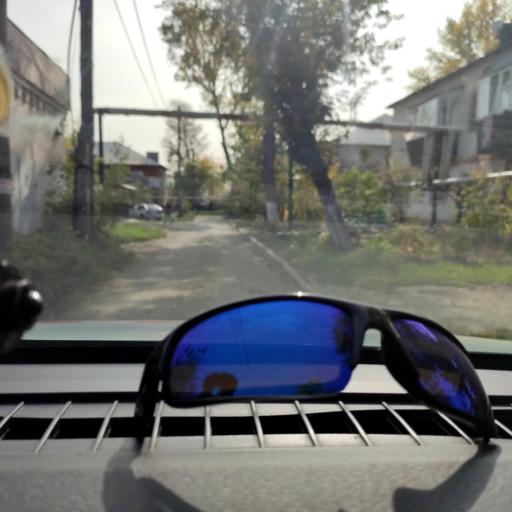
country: RU
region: Samara
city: Samara
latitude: 53.1332
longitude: 50.1211
